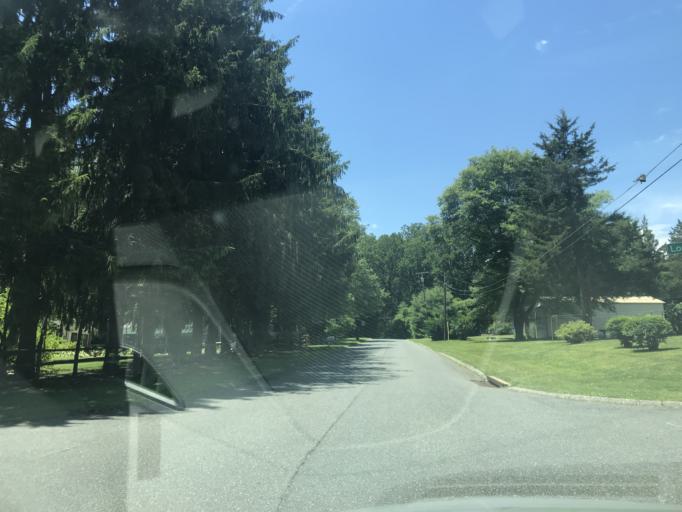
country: US
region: Maryland
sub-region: Baltimore County
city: Kingsville
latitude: 39.4692
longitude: -76.4488
